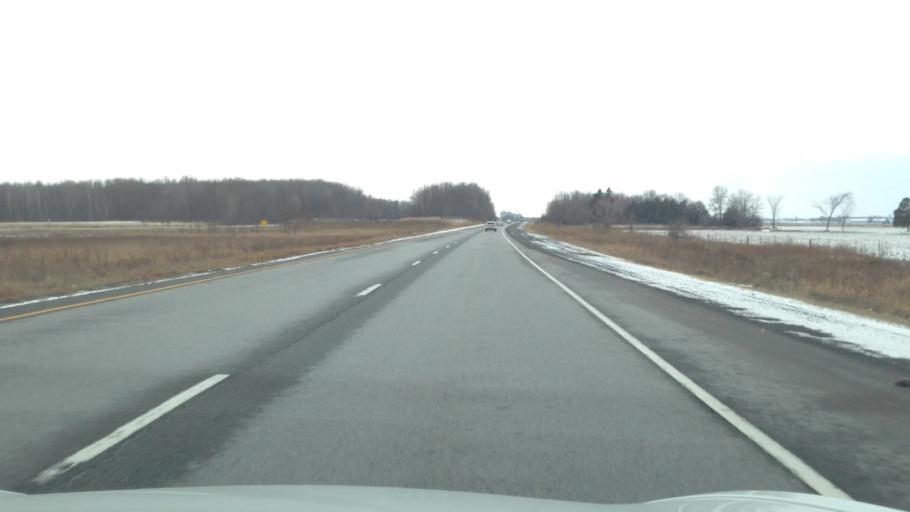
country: CA
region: Ontario
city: Casselman
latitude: 45.3703
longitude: -74.8557
